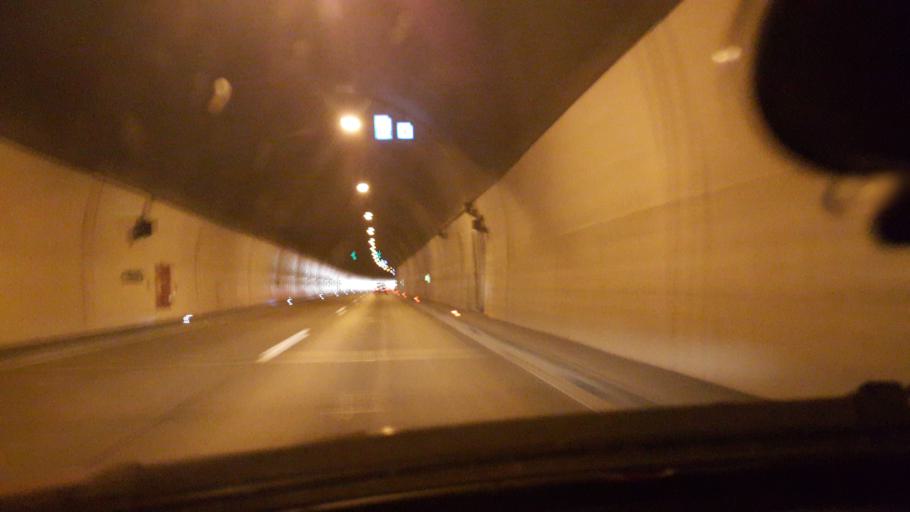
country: SI
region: Slovenska Konjice
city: Slovenske Konjice
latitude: 46.3146
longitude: 15.4579
